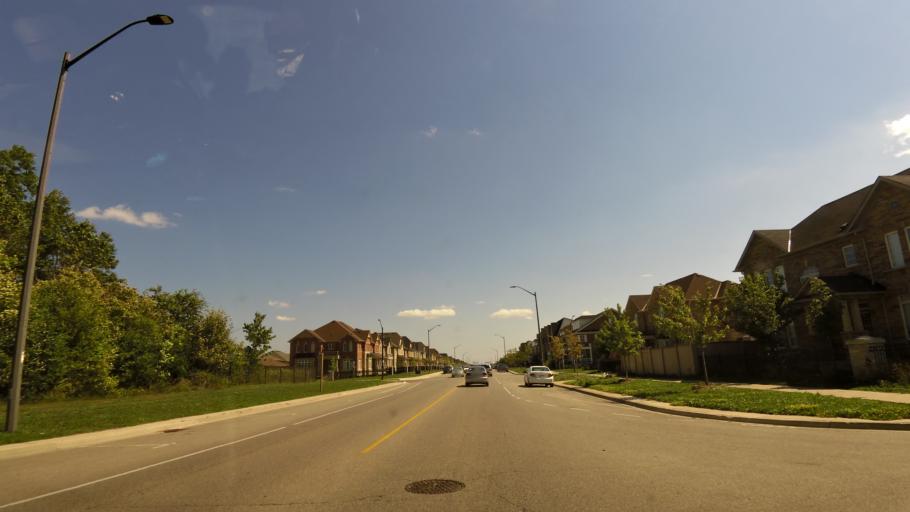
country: CA
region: Ontario
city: Mississauga
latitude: 43.5568
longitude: -79.7389
